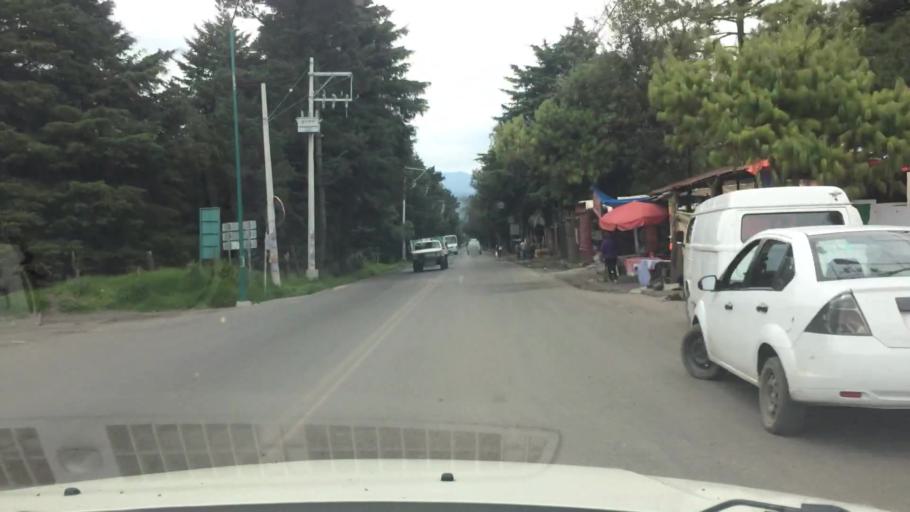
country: MX
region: Mexico City
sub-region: Tlalpan
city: Lomas de Tepemecatl
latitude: 19.2383
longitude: -99.2356
